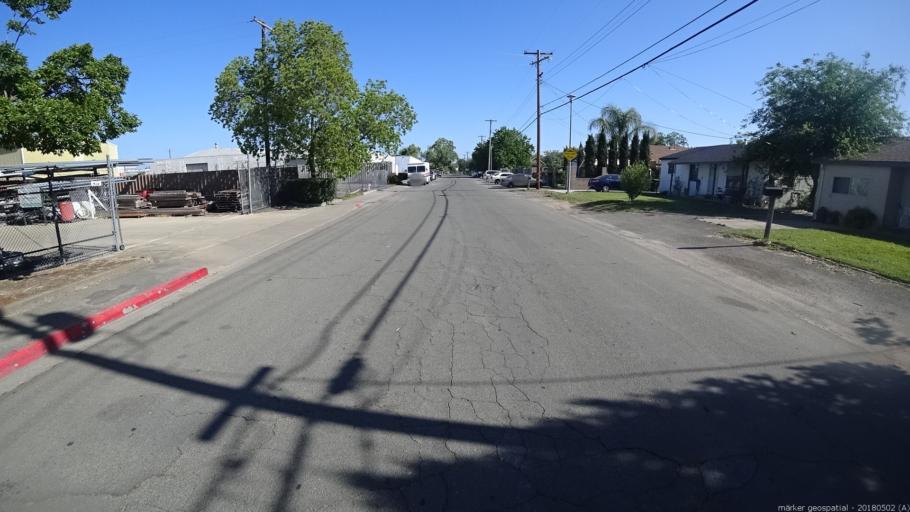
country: US
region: California
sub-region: Sacramento County
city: Arden-Arcade
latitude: 38.6171
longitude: -121.4254
